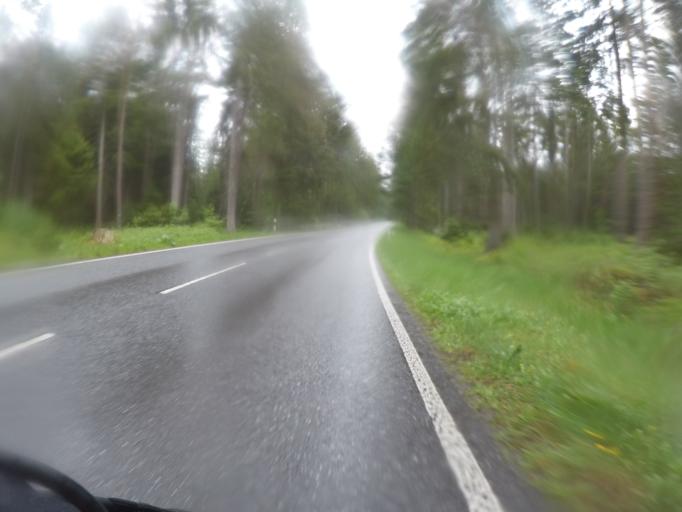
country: DE
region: Schleswig-Holstein
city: Hartenholm
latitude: 53.9328
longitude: 10.0877
